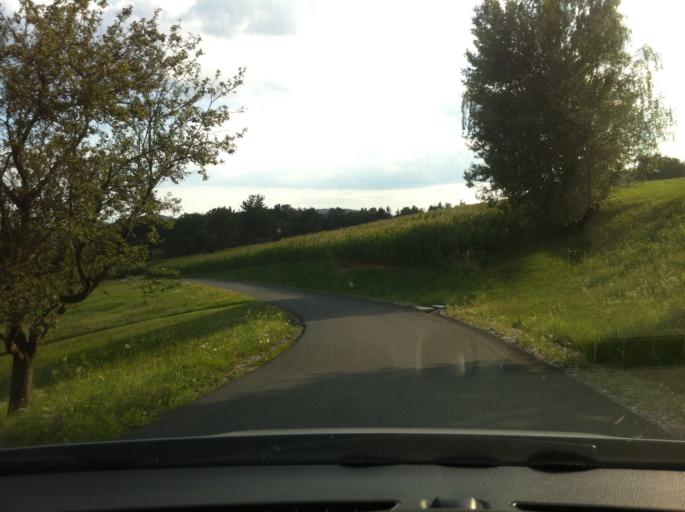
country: AT
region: Styria
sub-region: Politischer Bezirk Hartberg-Fuerstenfeld
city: Stubenberg
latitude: 47.2474
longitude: 15.8271
